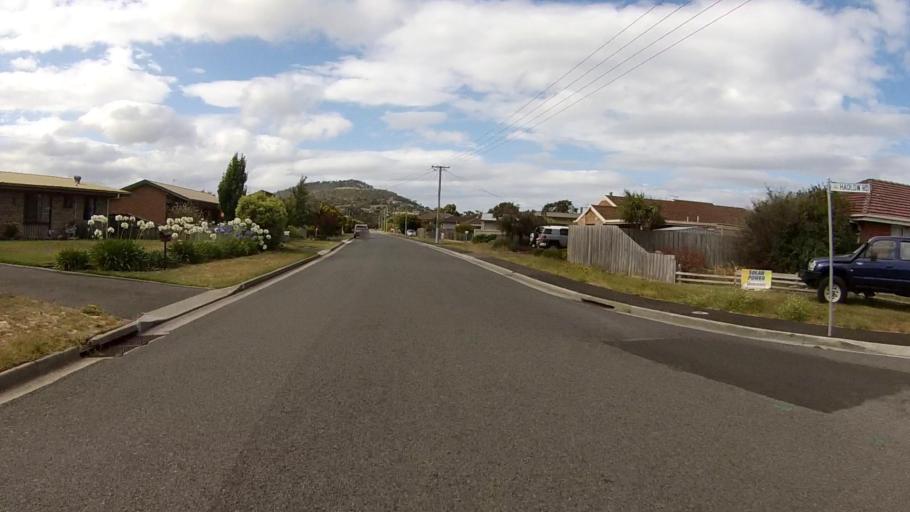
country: AU
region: Tasmania
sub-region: Clarence
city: Lauderdale
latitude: -42.8973
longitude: 147.4954
